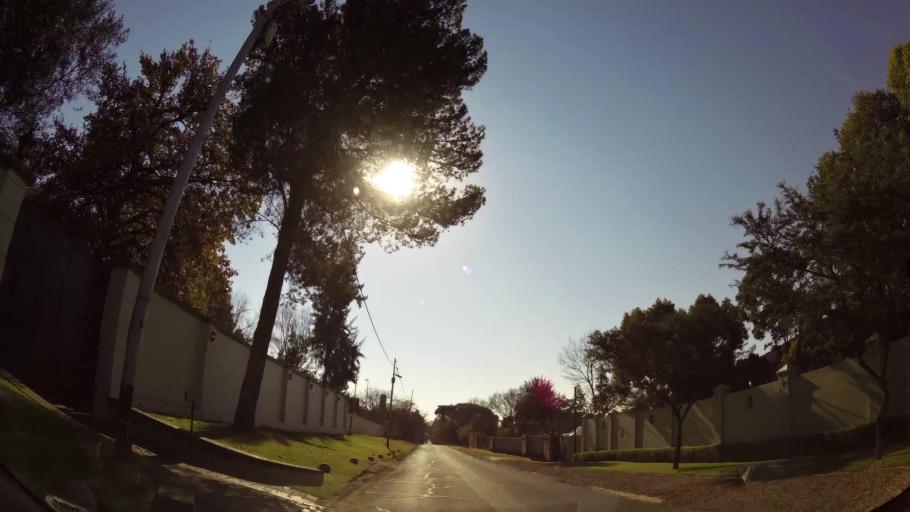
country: ZA
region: Gauteng
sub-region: City of Johannesburg Metropolitan Municipality
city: Midrand
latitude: -26.0613
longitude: 28.0409
